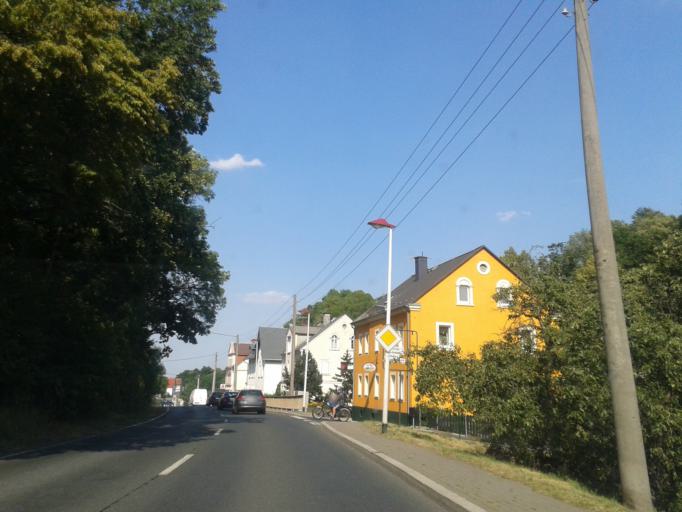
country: DE
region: Saxony
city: Niederschona
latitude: 51.0000
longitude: 13.4571
